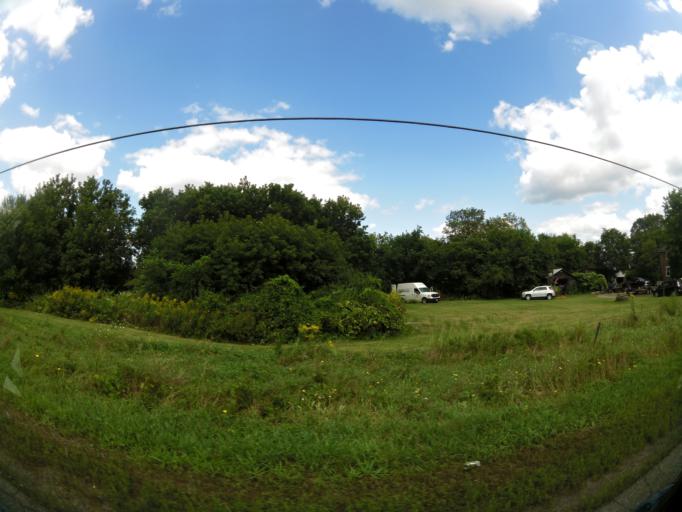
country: CA
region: Ontario
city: Ottawa
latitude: 45.3945
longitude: -75.5633
